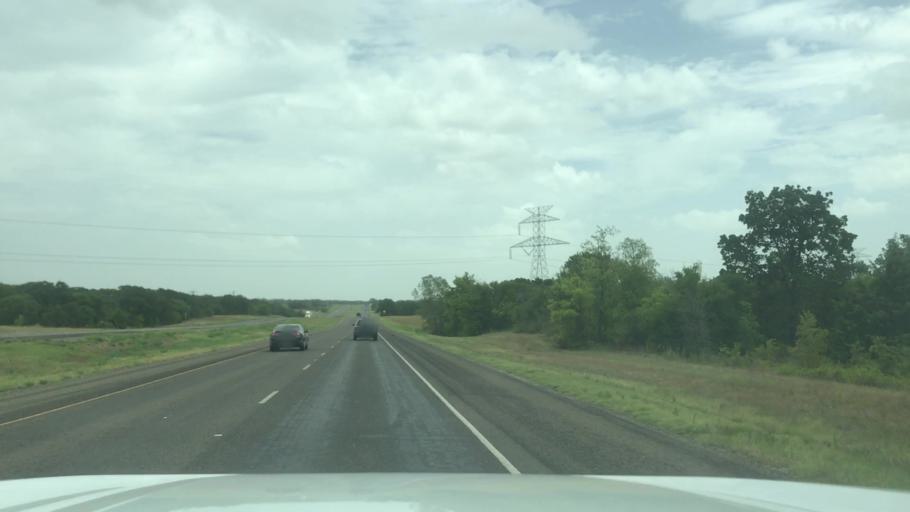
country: US
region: Texas
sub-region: McLennan County
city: Riesel
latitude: 31.5070
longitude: -96.9477
